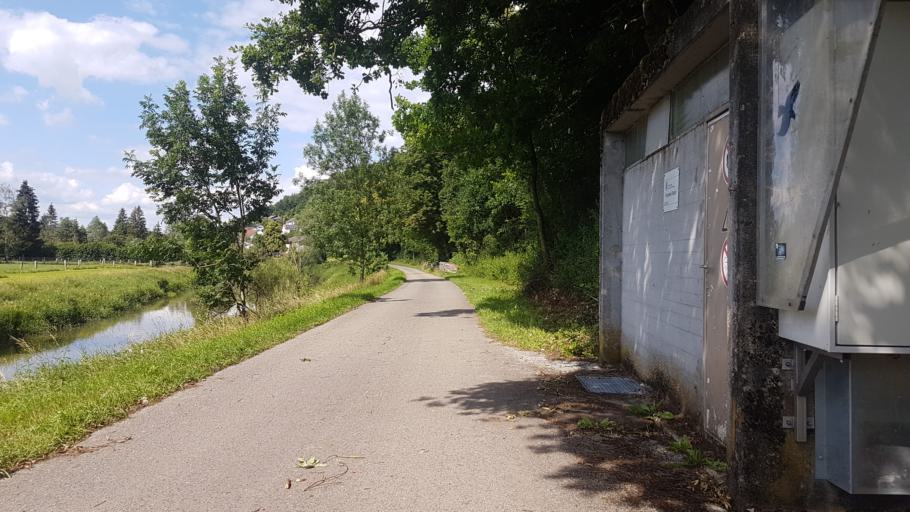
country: DE
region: Bavaria
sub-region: Regierungsbezirk Mittelfranken
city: Treuchtlingen
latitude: 48.9407
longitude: 10.9338
